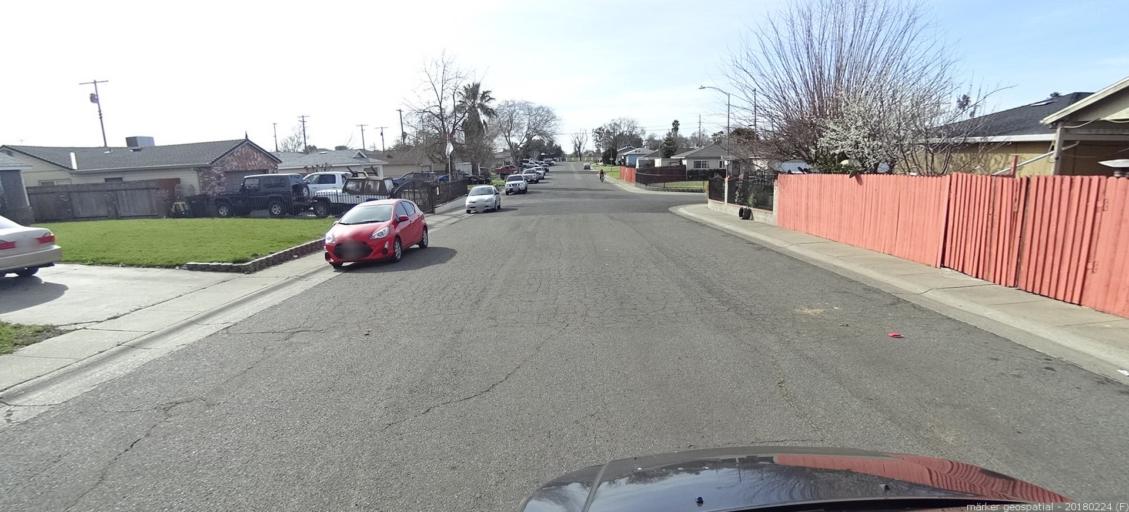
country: US
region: California
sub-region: Sacramento County
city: Elverta
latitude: 38.7003
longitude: -121.4596
